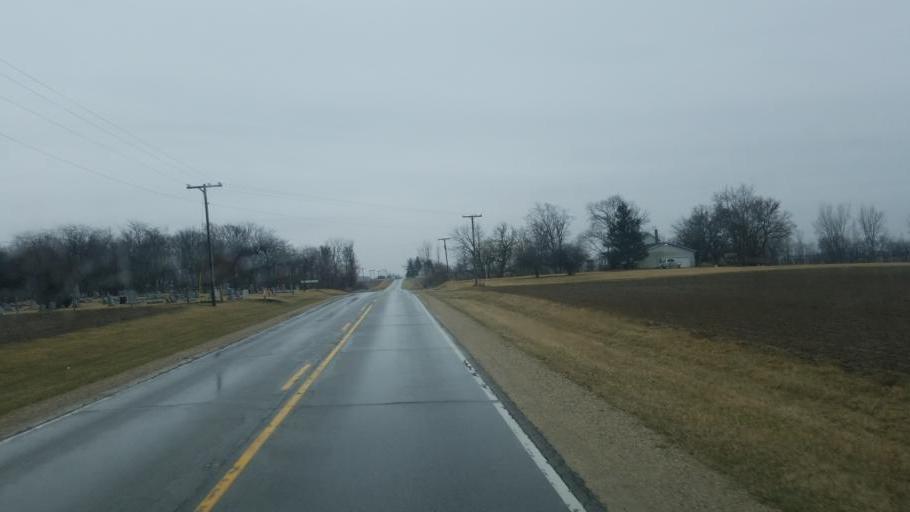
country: US
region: Indiana
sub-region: Adams County
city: Berne
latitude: 40.6369
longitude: -85.0414
